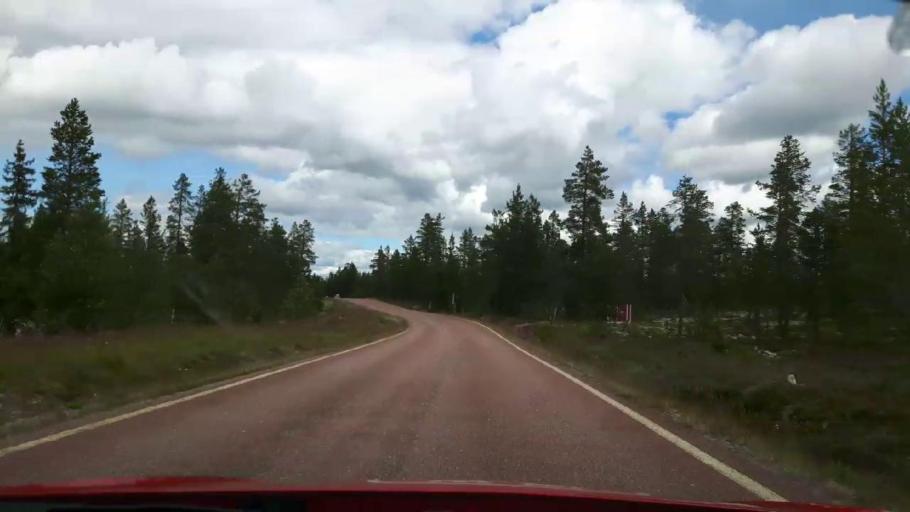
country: NO
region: Hedmark
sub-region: Trysil
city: Innbygda
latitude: 61.9218
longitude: 13.0166
